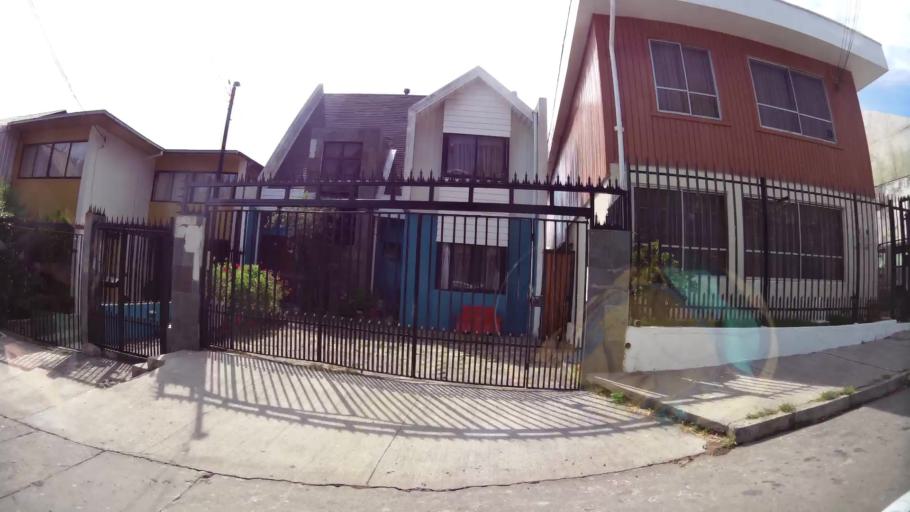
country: CL
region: Biobio
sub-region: Provincia de Concepcion
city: Talcahuano
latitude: -36.7168
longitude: -73.1108
